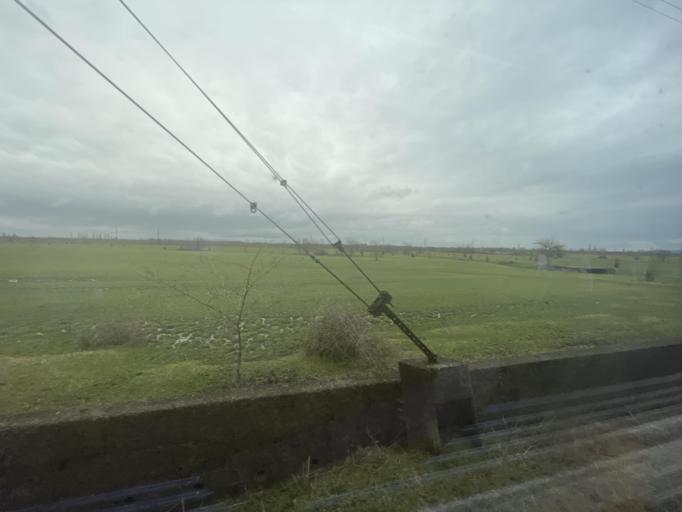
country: GE
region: Guria
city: Lanchkhuti
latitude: 42.0859
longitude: 42.0668
